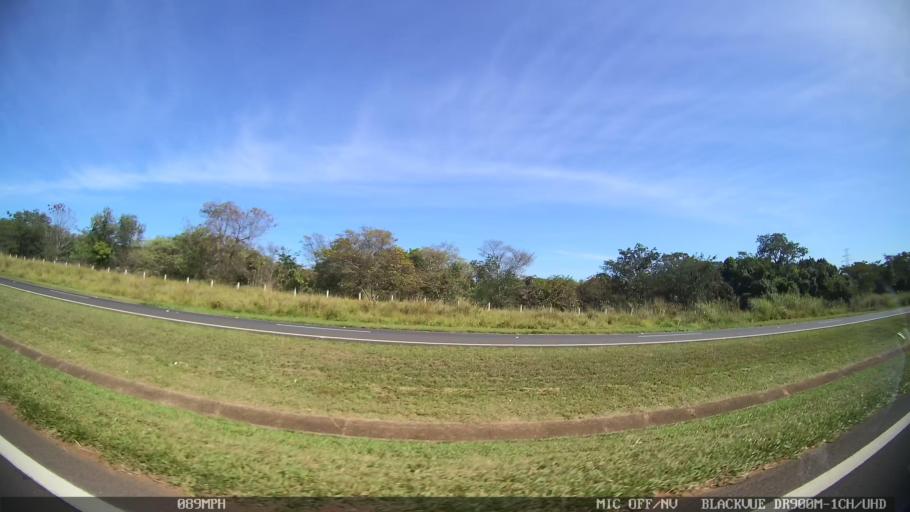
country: BR
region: Sao Paulo
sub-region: Porto Ferreira
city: Porto Ferreira
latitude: -21.9275
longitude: -47.4699
